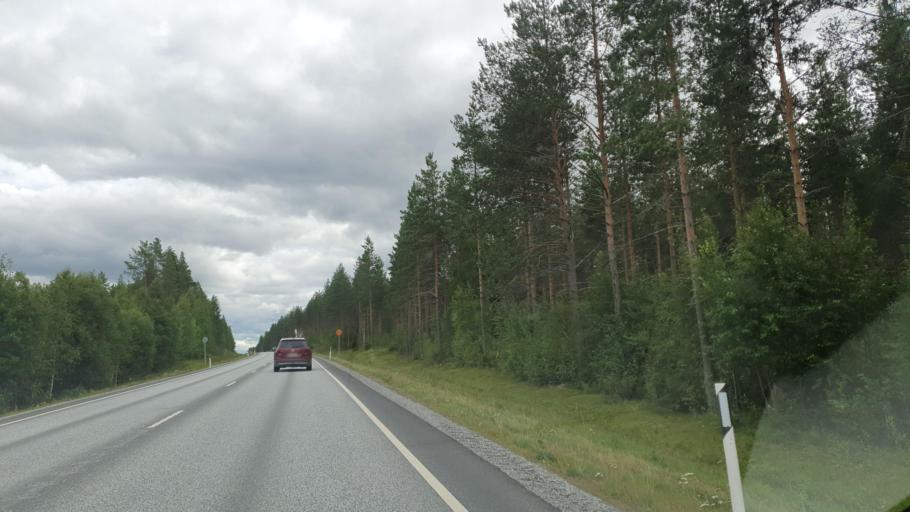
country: FI
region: Northern Savo
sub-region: Ylae-Savo
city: Sonkajaervi
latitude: 63.8978
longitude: 27.4033
